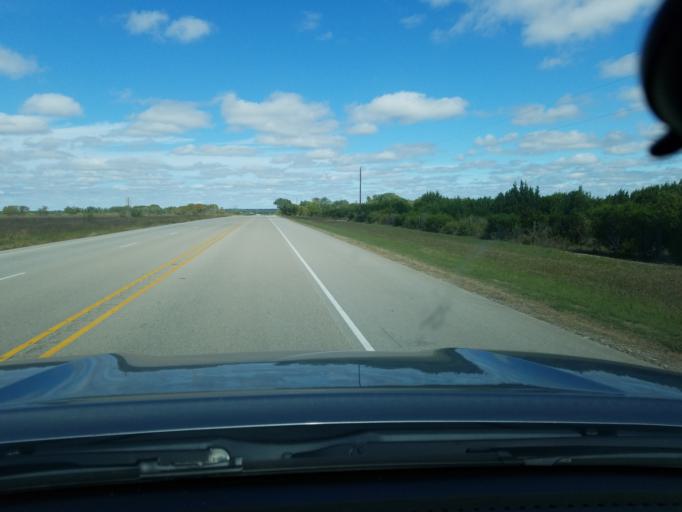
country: US
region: Texas
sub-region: Hamilton County
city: Hamilton
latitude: 31.5704
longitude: -98.1582
